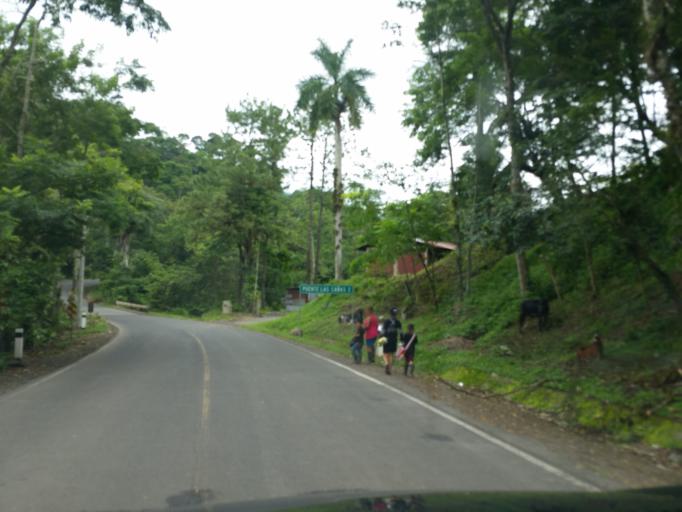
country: NI
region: Matagalpa
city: San Ramon
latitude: 12.9916
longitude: -85.8324
